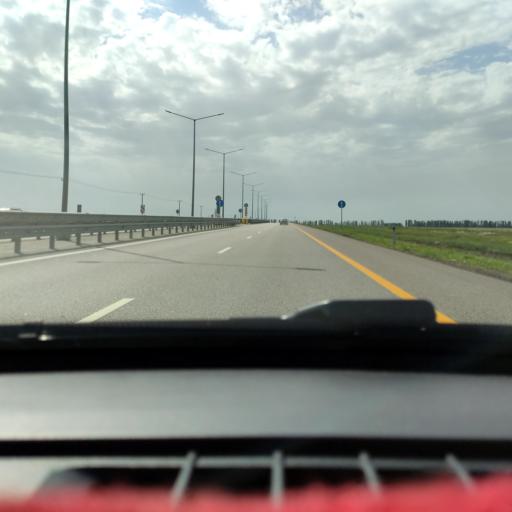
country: RU
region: Voronezj
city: Kashirskoye
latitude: 51.4901
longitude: 39.5312
